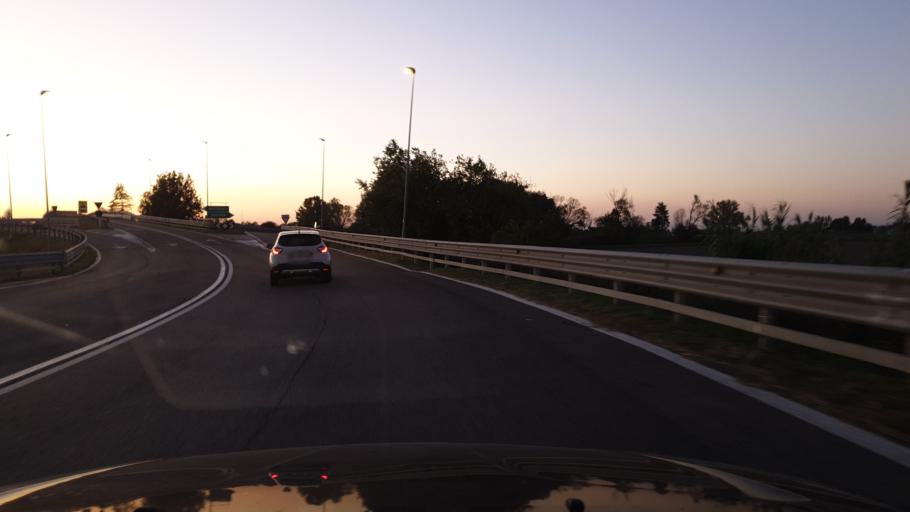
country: IT
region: Emilia-Romagna
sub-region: Provincia di Bologna
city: Altedo
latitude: 44.6866
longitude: 11.4816
